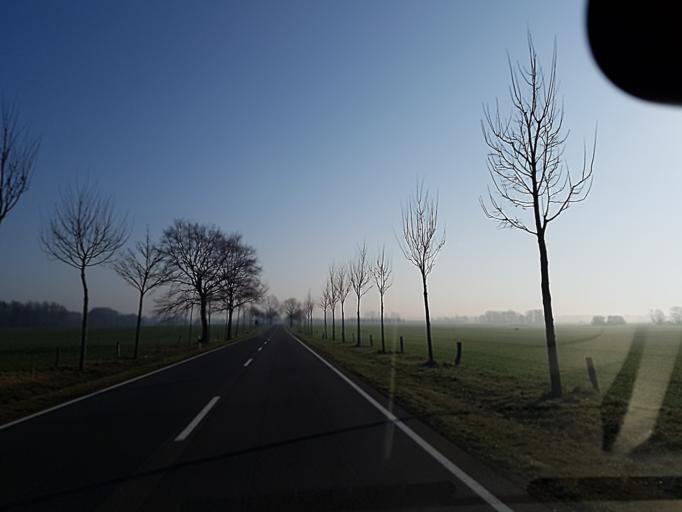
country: DE
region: Brandenburg
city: Sallgast
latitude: 51.6287
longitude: 13.8406
